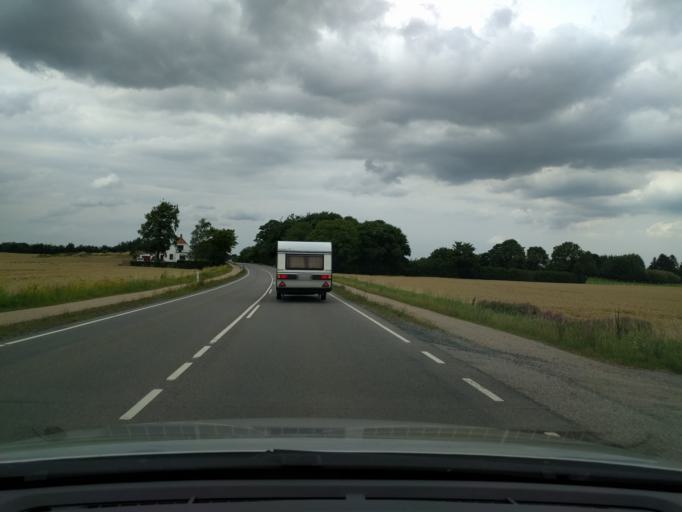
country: DK
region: Zealand
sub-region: Ringsted Kommune
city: Ringsted
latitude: 55.4126
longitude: 11.8347
